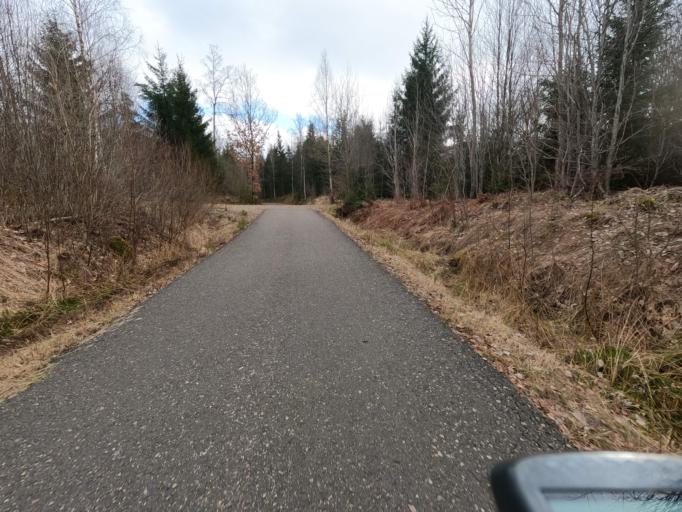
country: SE
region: Joenkoeping
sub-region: Varnamo Kommun
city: Rydaholm
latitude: 56.8371
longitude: 14.2404
